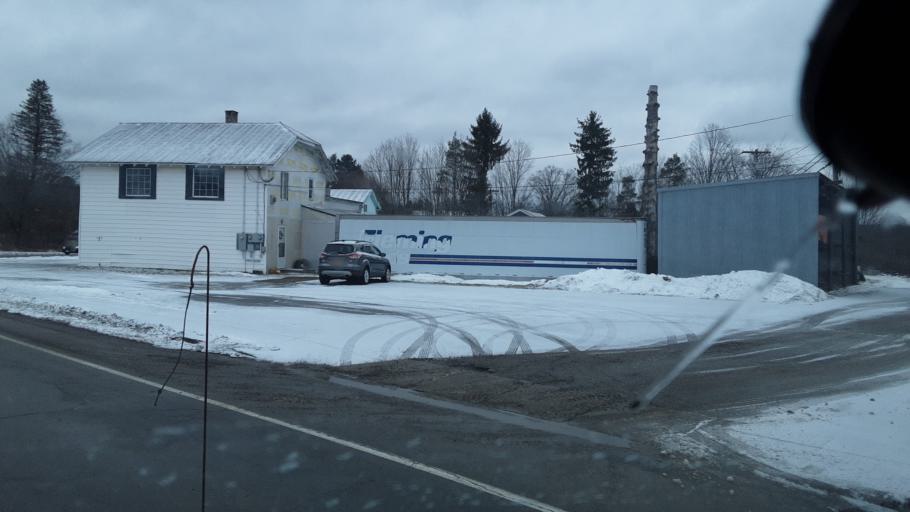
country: US
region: New York
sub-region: Allegany County
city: Friendship
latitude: 42.2025
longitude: -78.1452
